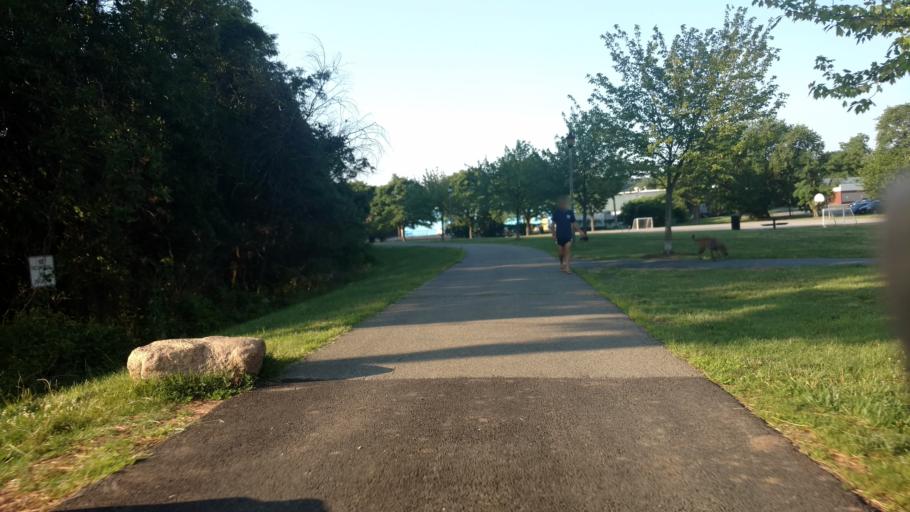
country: US
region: Virginia
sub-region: City of Alexandria
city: Alexandria
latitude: 38.8416
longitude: -77.0610
